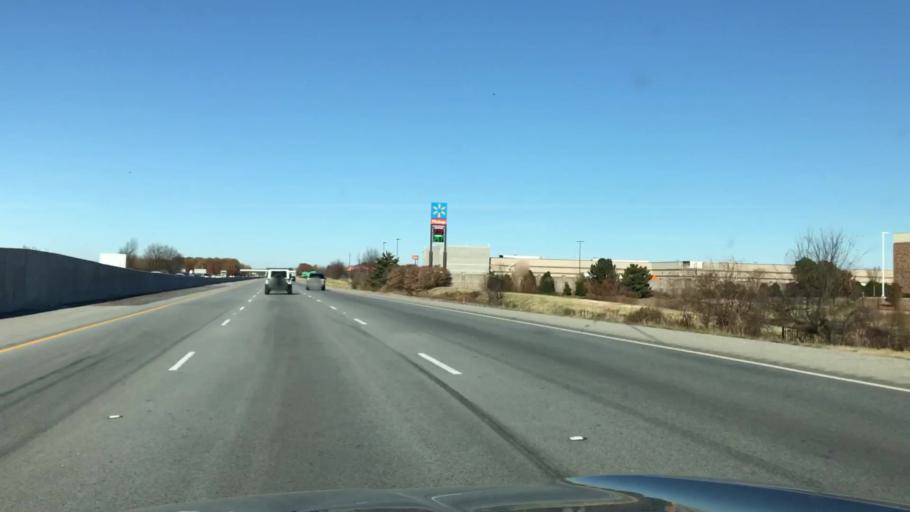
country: US
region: Arkansas
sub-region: Benton County
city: Lowell
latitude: 36.2762
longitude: -94.1511
